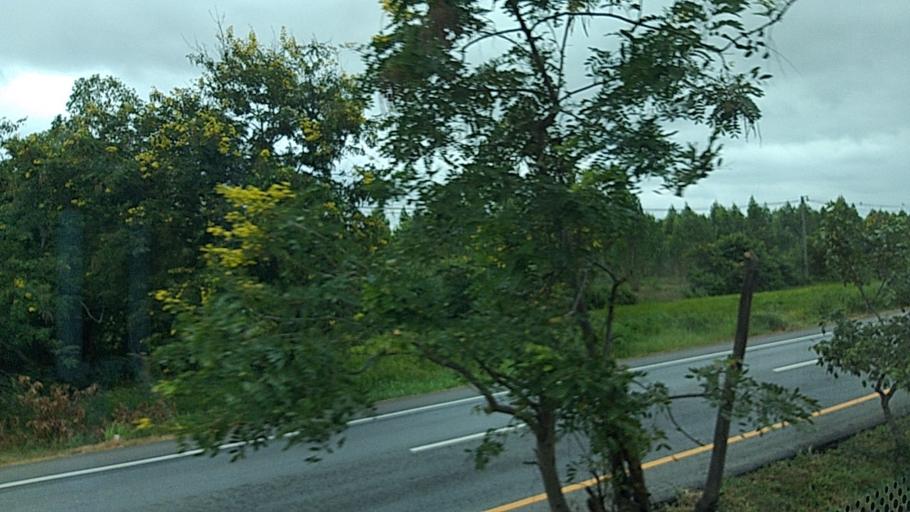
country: TH
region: Khon Kaen
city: Phon
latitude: 15.7275
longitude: 102.5943
